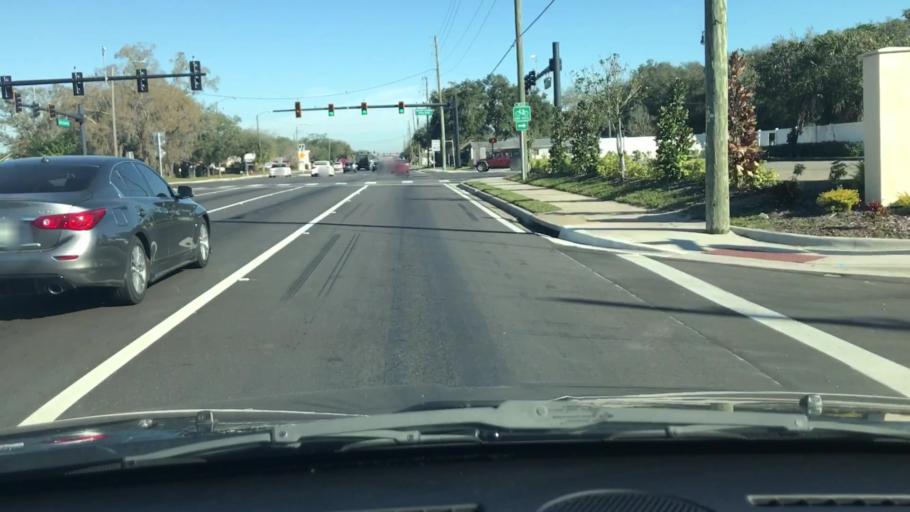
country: US
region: Florida
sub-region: Osceola County
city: Kissimmee
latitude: 28.2966
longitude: -81.4159
